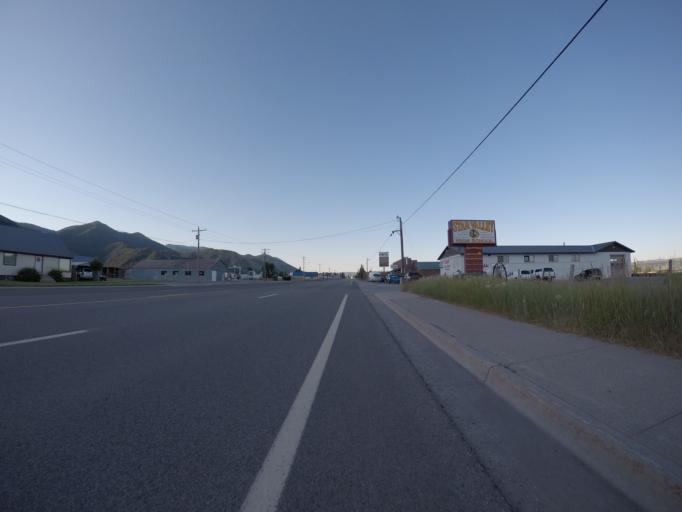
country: US
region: Wyoming
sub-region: Lincoln County
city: Afton
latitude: 42.7406
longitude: -110.9335
